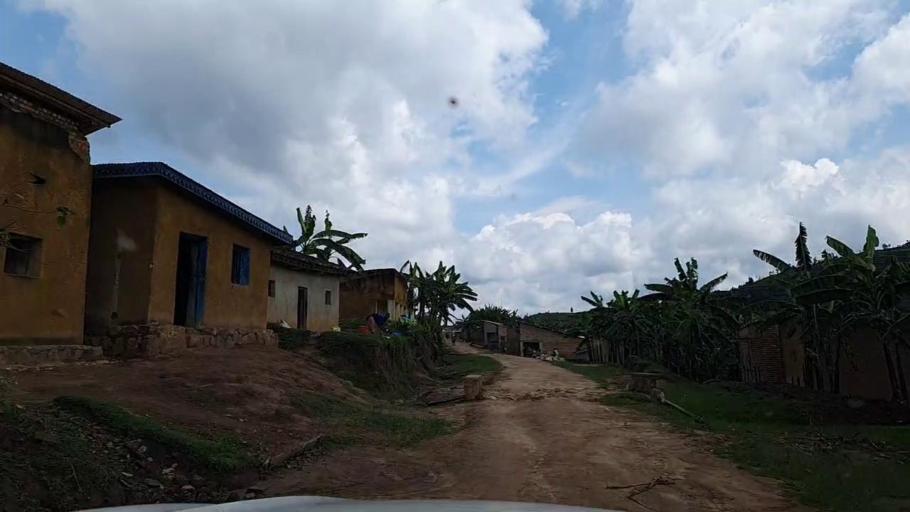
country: RW
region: Southern Province
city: Gikongoro
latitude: -2.3954
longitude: 29.5530
